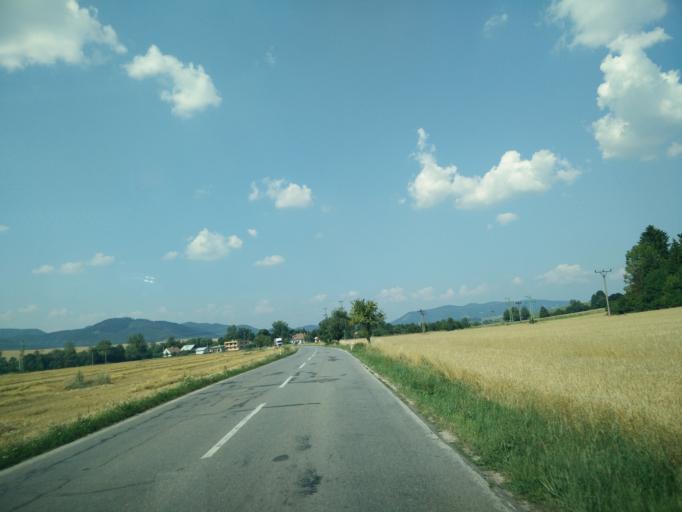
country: SK
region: Zilinsky
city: Rajec
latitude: 49.0625
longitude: 18.6278
